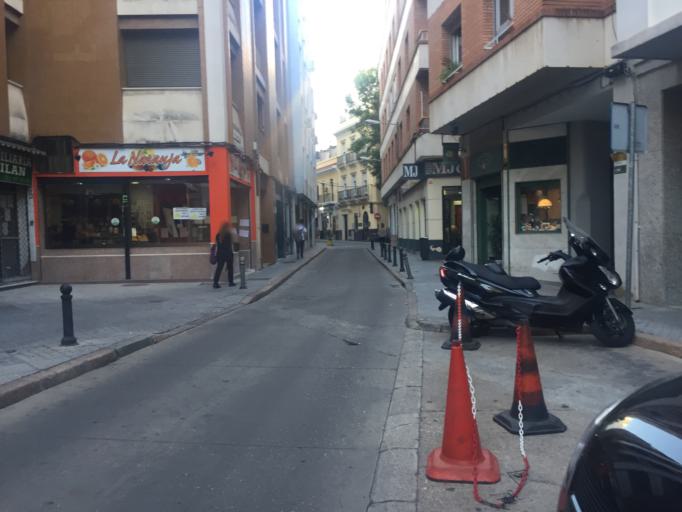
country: ES
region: Andalusia
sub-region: Province of Cordoba
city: Cordoba
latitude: 37.8855
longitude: -4.7840
